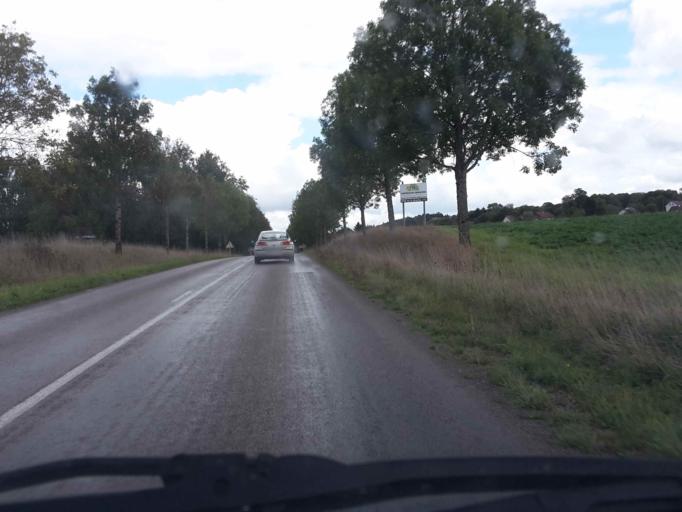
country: FR
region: Franche-Comte
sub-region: Departement du Doubs
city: Nancray
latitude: 47.2438
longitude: 6.1692
